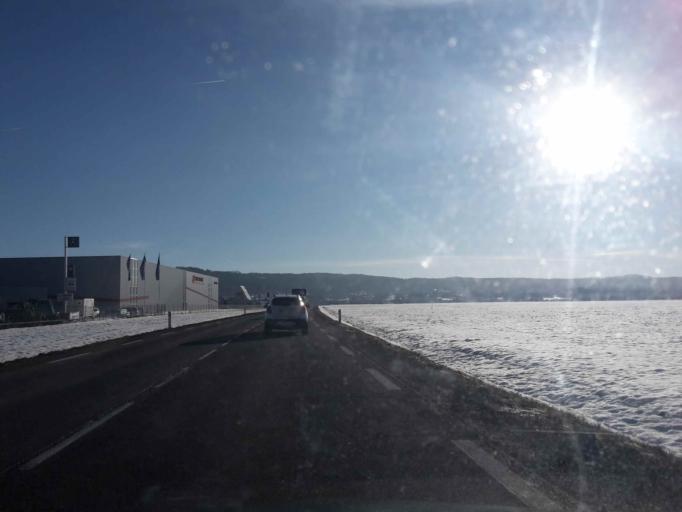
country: FR
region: Franche-Comte
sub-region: Departement du Doubs
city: Pontarlier
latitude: 46.9071
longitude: 6.3312
